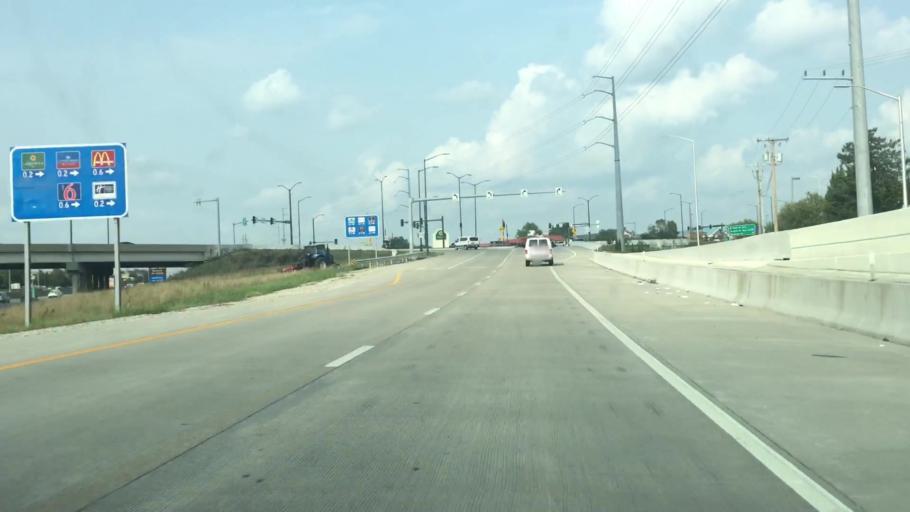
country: US
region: Kansas
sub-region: Johnson County
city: Lenexa
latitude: 38.9554
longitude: -94.7331
